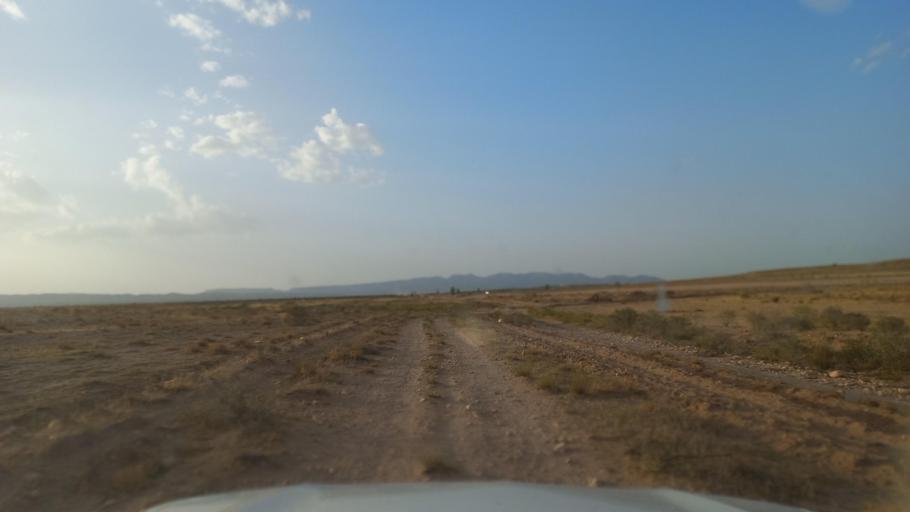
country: TN
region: Al Qasrayn
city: Sbiba
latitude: 35.3077
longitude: 9.0738
